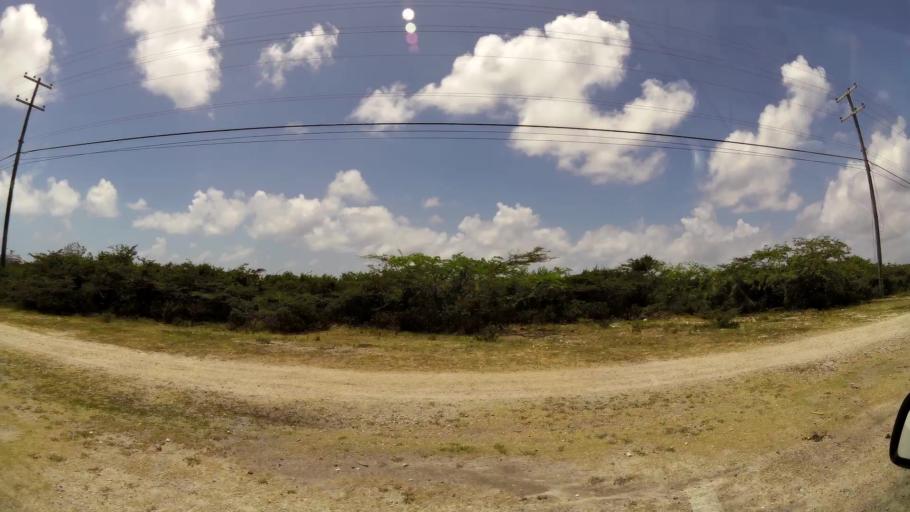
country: TC
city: Cockburn Town
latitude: 21.4425
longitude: -71.1490
